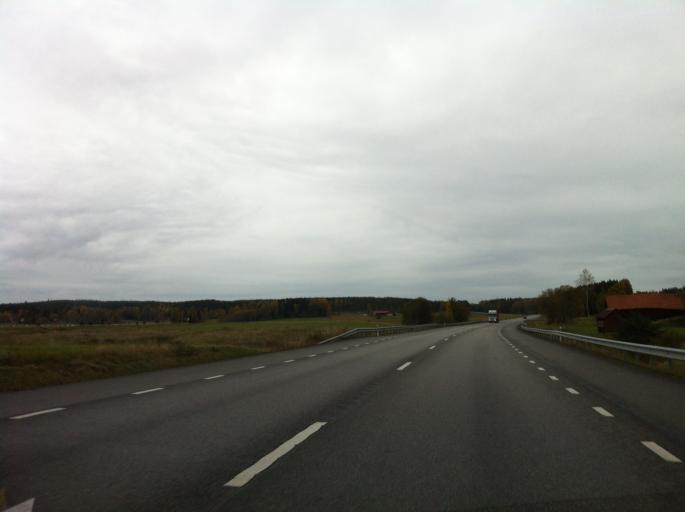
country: SE
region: OErebro
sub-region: Lindesbergs Kommun
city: Stora
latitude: 59.7559
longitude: 15.1449
